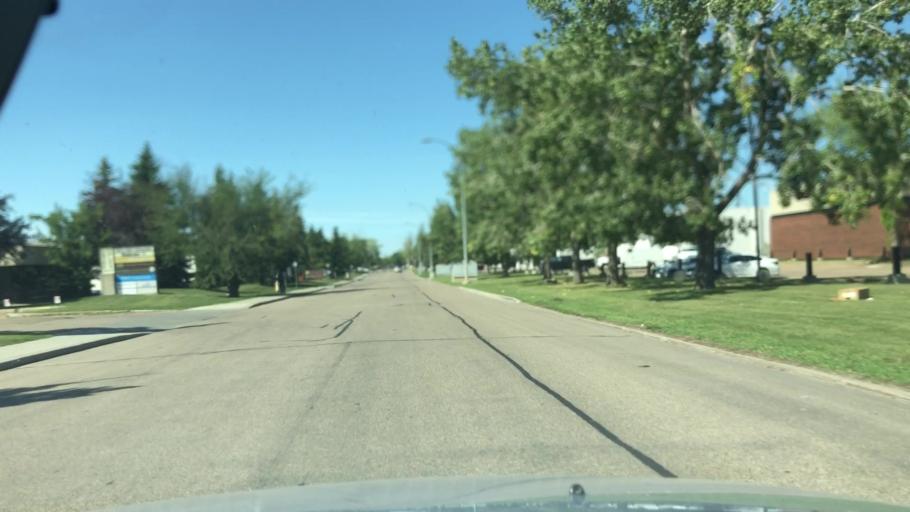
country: CA
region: Alberta
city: Edmonton
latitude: 53.5309
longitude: -113.4149
